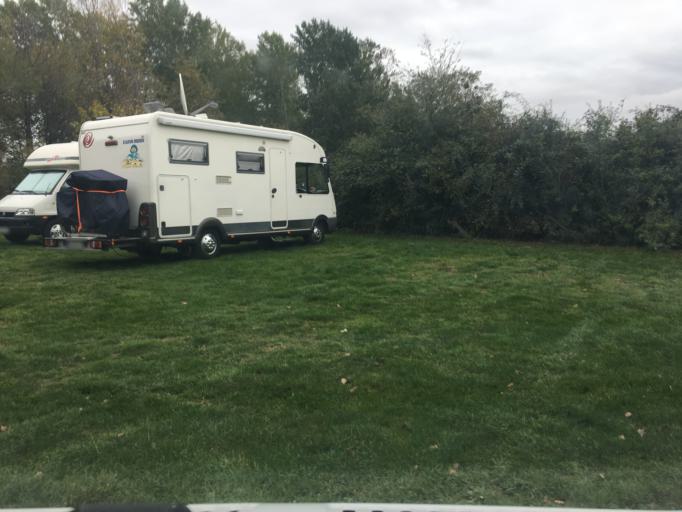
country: DE
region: North Rhine-Westphalia
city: Zulpich
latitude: 50.6764
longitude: 6.6596
